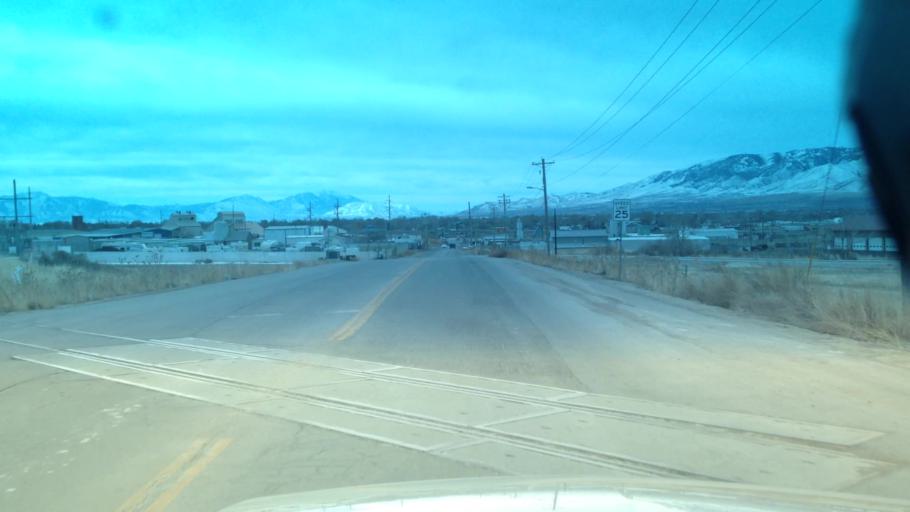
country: US
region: Utah
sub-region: Utah County
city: Lehi
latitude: 40.4221
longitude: -111.8688
